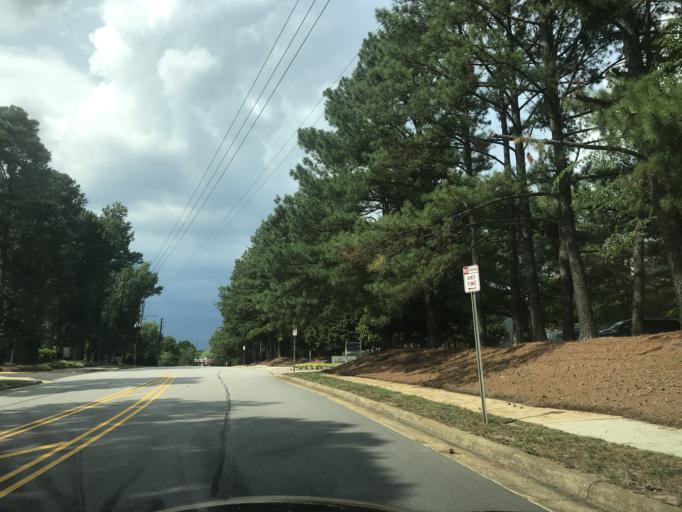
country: US
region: North Carolina
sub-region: Wake County
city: West Raleigh
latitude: 35.8957
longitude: -78.6530
